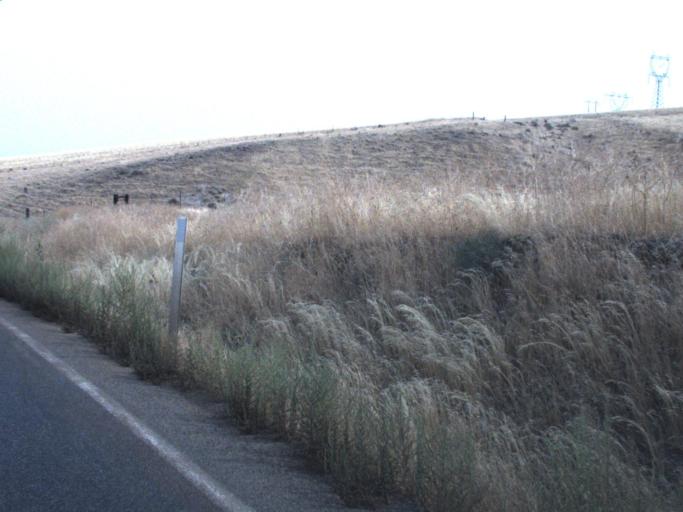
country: US
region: Washington
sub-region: Grant County
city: Desert Aire
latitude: 46.4950
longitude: -119.9039
